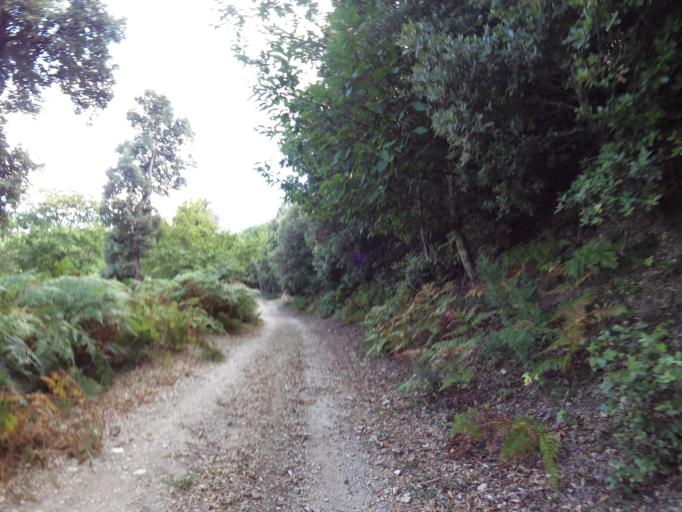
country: IT
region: Calabria
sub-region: Provincia di Reggio Calabria
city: Pazzano
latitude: 38.4763
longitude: 16.4059
